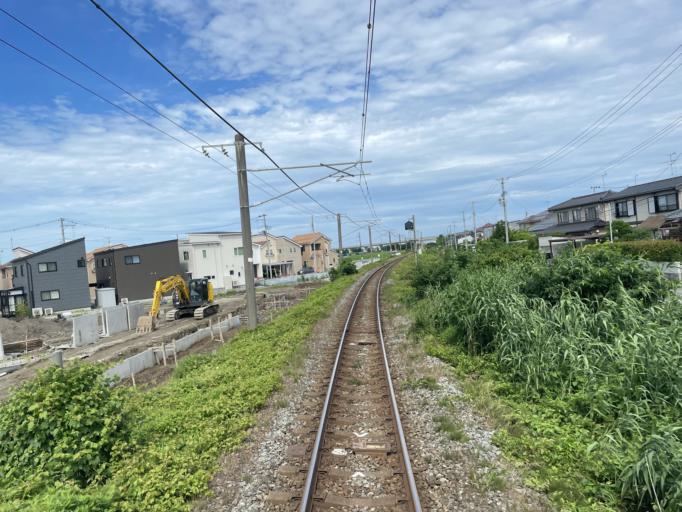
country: JP
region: Niigata
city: Suibara
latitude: 37.9156
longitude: 139.2074
